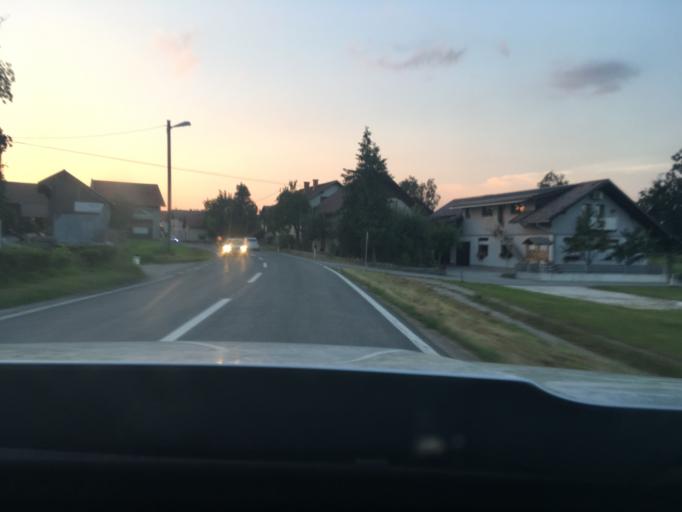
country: SI
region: Ribnica
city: Ribnica
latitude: 45.7190
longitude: 14.7452
